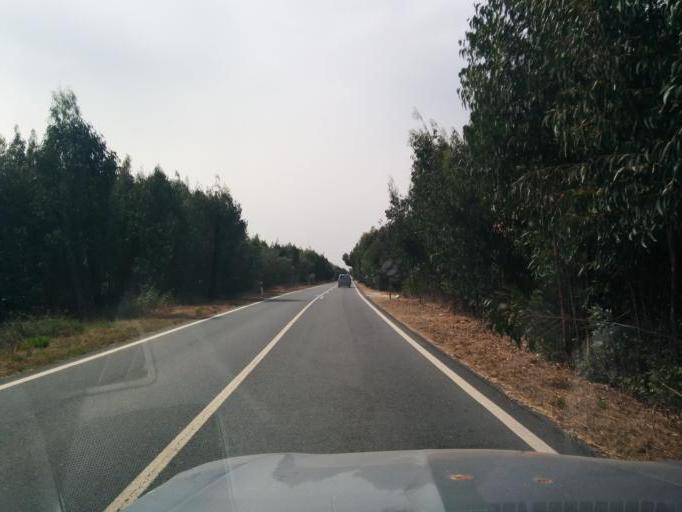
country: PT
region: Beja
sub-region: Odemira
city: Vila Nova de Milfontes
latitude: 37.6698
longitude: -8.7595
